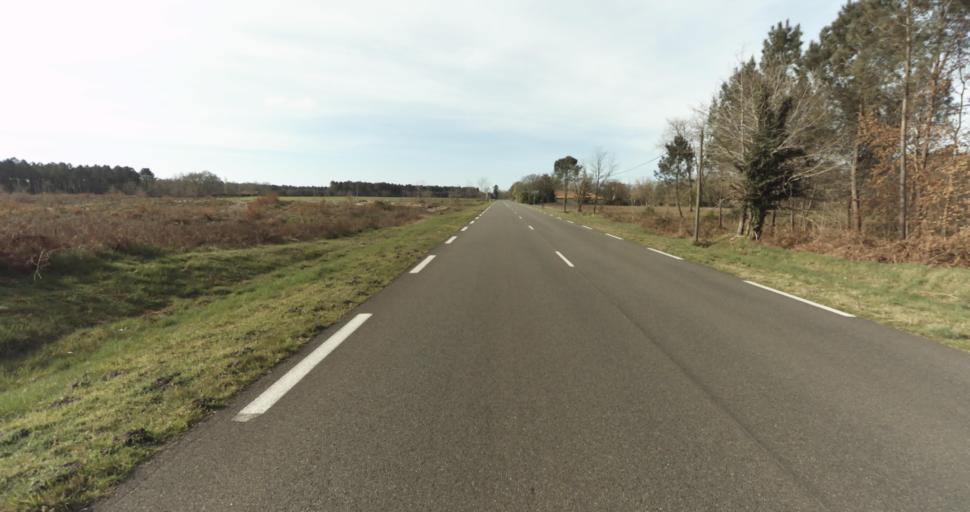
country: FR
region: Aquitaine
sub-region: Departement des Landes
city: Roquefort
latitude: 44.1125
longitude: -0.2995
